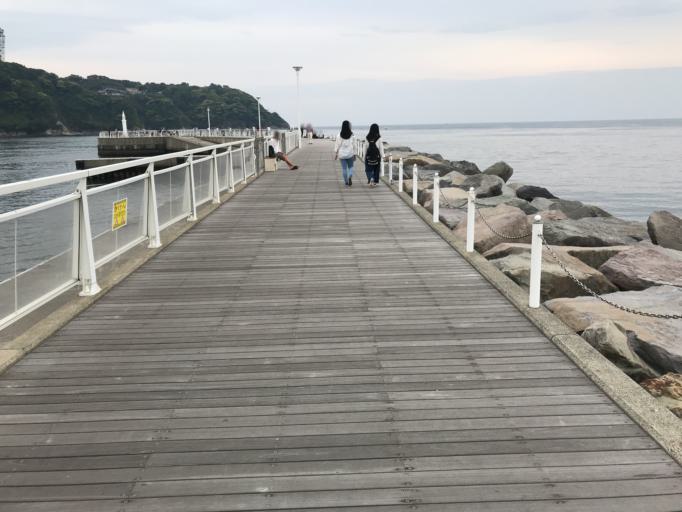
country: JP
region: Kanagawa
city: Fujisawa
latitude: 35.3059
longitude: 139.4795
